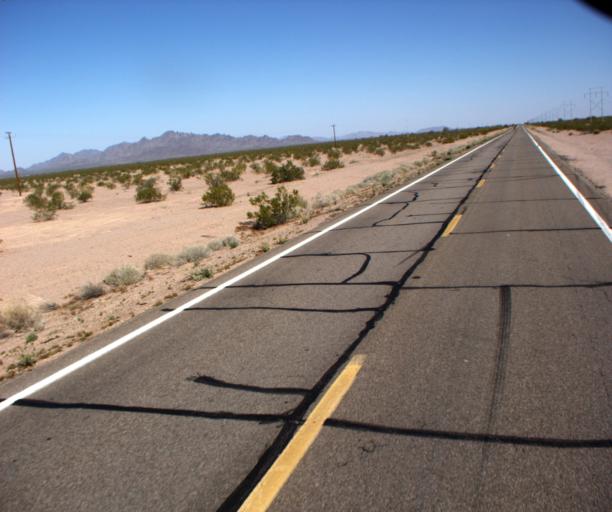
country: US
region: Arizona
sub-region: La Paz County
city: Quartzsite
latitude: 33.4170
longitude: -114.2170
